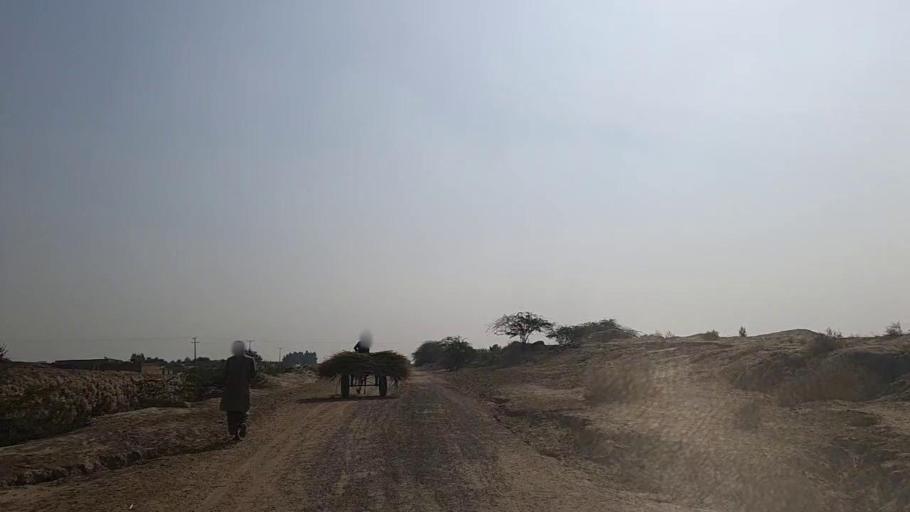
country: PK
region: Sindh
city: Daur
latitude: 26.4663
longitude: 68.4670
